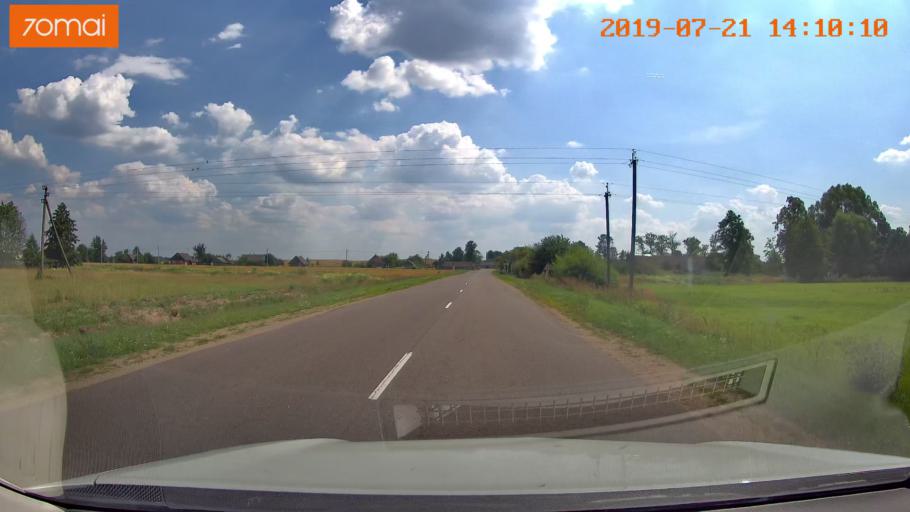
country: BY
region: Grodnenskaya
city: Karelichy
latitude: 53.6656
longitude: 26.1342
